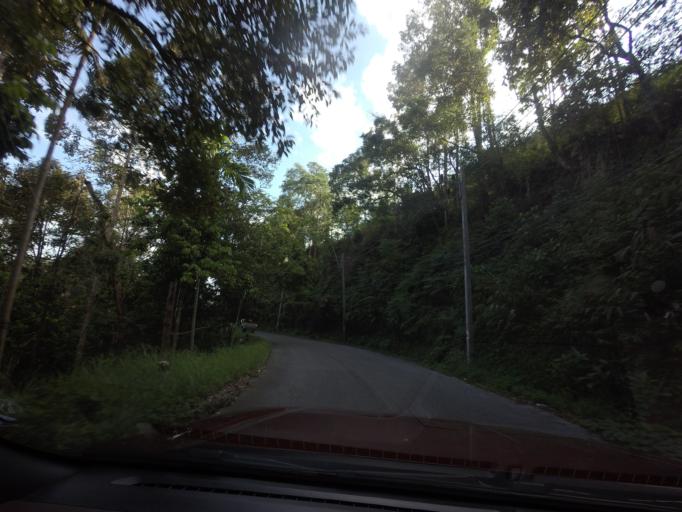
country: TH
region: Yala
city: Than To
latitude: 6.1394
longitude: 101.2946
